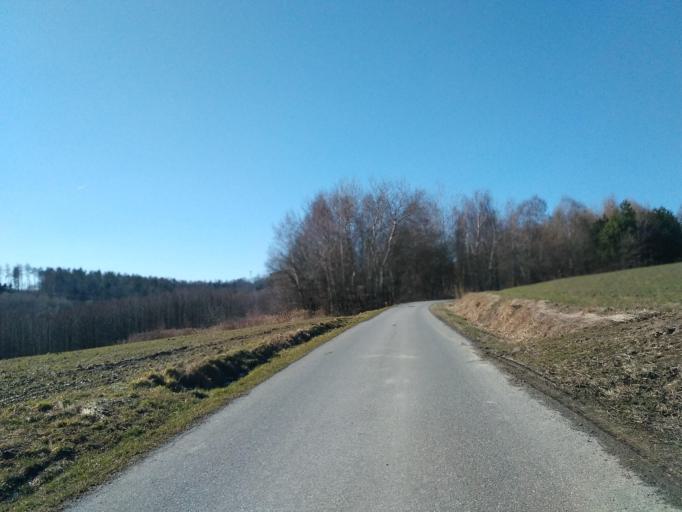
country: PL
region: Subcarpathian Voivodeship
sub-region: Powiat rzeszowski
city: Lutoryz
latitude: 49.9529
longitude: 21.8948
